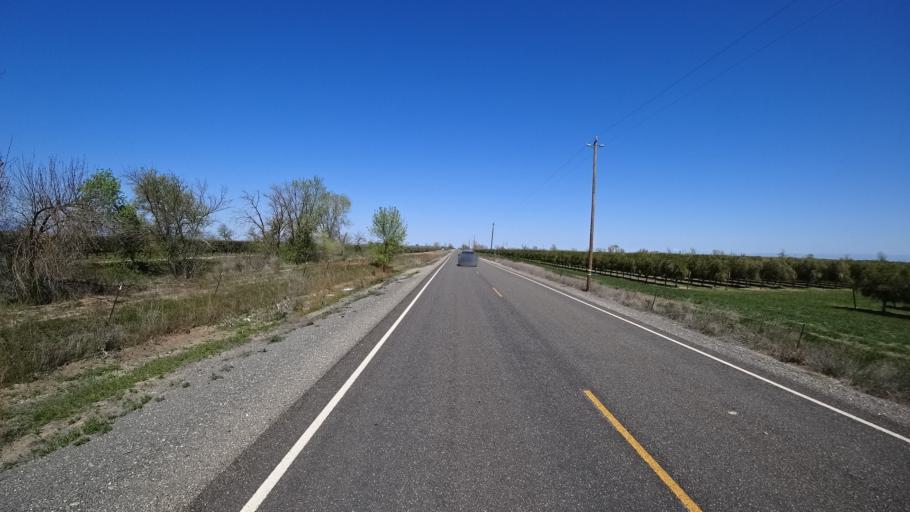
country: US
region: California
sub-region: Glenn County
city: Willows
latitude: 39.6072
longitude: -122.2499
